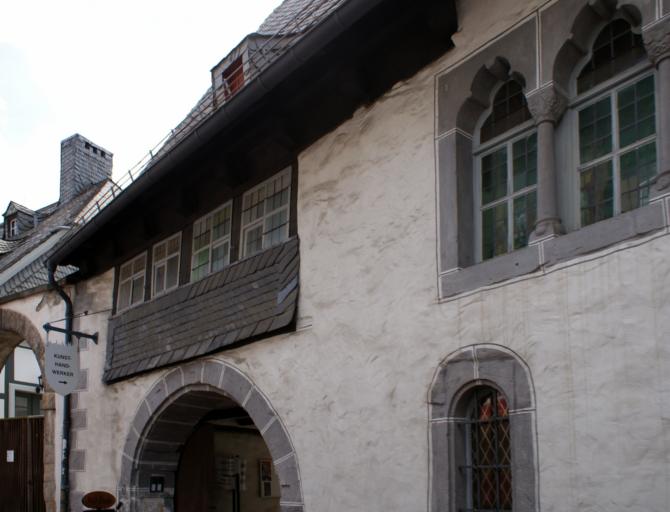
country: DE
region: Lower Saxony
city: Goslar
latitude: 51.9045
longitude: 10.4249
